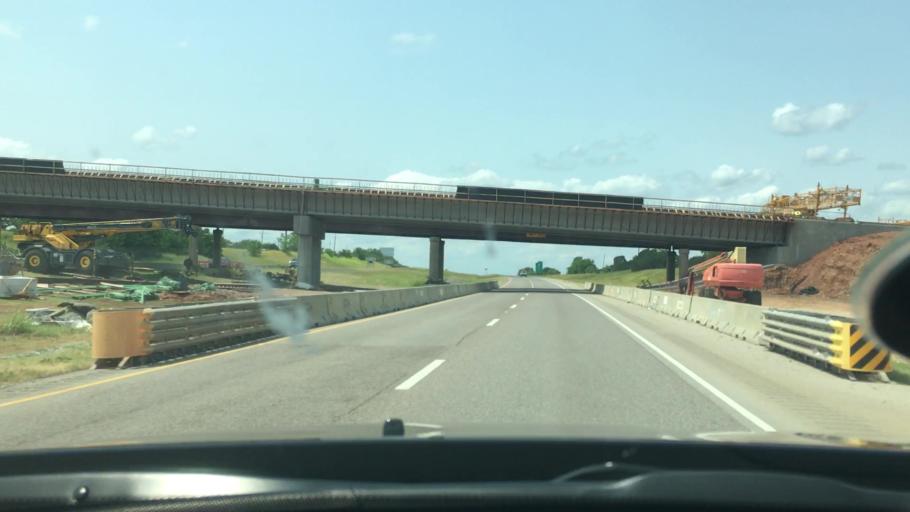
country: US
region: Oklahoma
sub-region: Murray County
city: Davis
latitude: 34.4874
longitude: -97.1606
